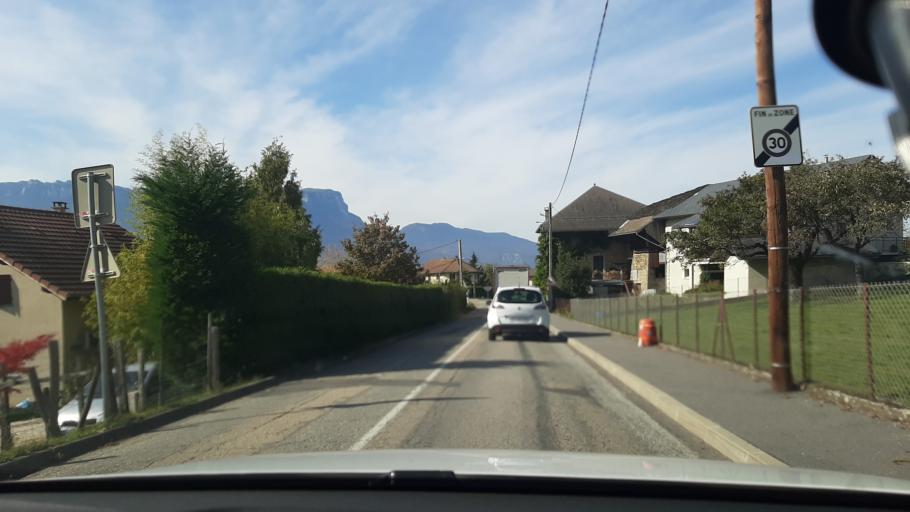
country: FR
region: Rhone-Alpes
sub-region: Departement de la Savoie
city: Montmelian
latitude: 45.4487
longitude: 6.0670
